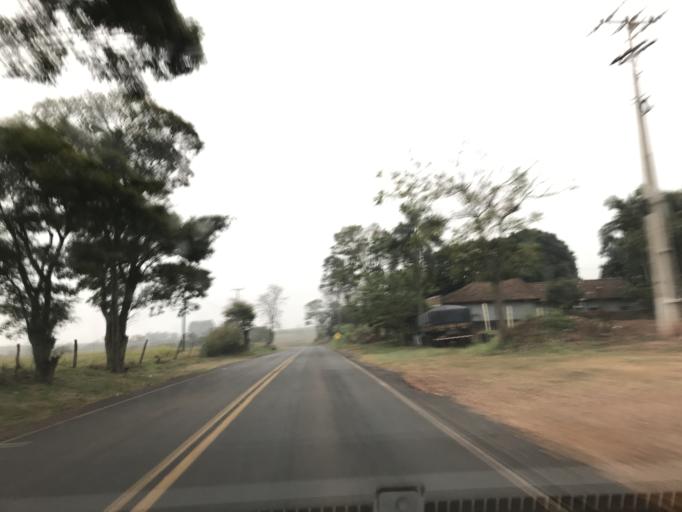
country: PY
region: Canindeyu
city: Salto del Guaira
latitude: -24.1306
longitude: -54.1131
